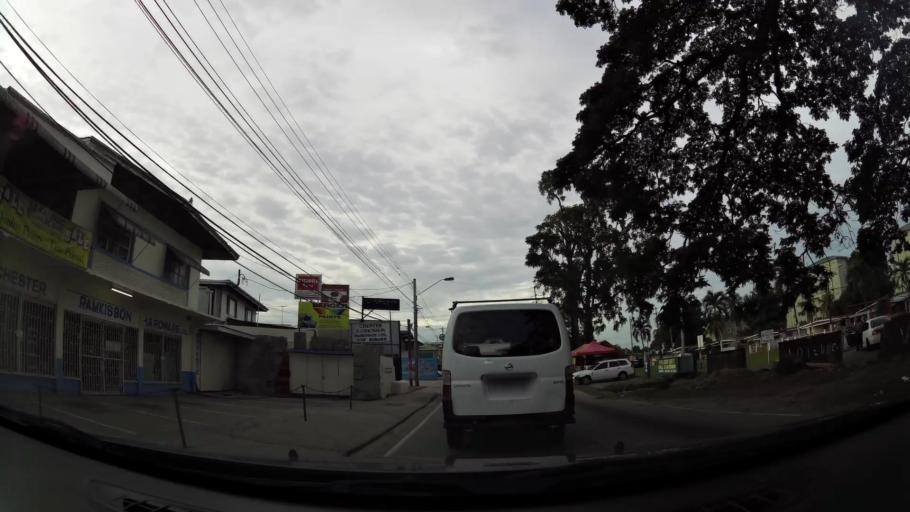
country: TT
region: Tunapuna/Piarco
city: Tunapuna
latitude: 10.6398
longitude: -61.4109
